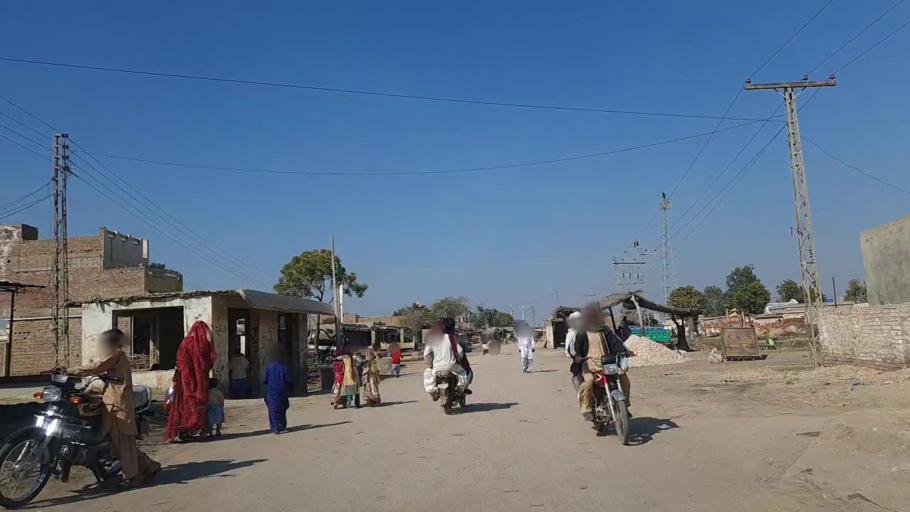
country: PK
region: Sindh
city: Nawabshah
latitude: 26.3517
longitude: 68.3656
